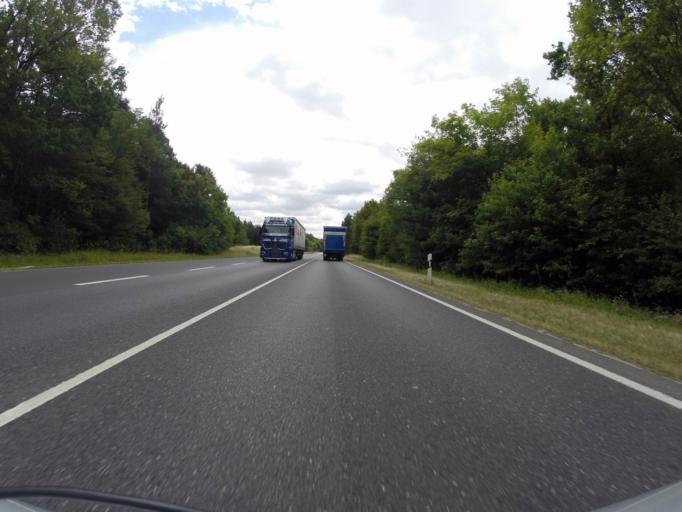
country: DE
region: Bavaria
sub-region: Regierungsbezirk Unterfranken
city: Schwebheim
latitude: 50.0125
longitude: 10.2381
